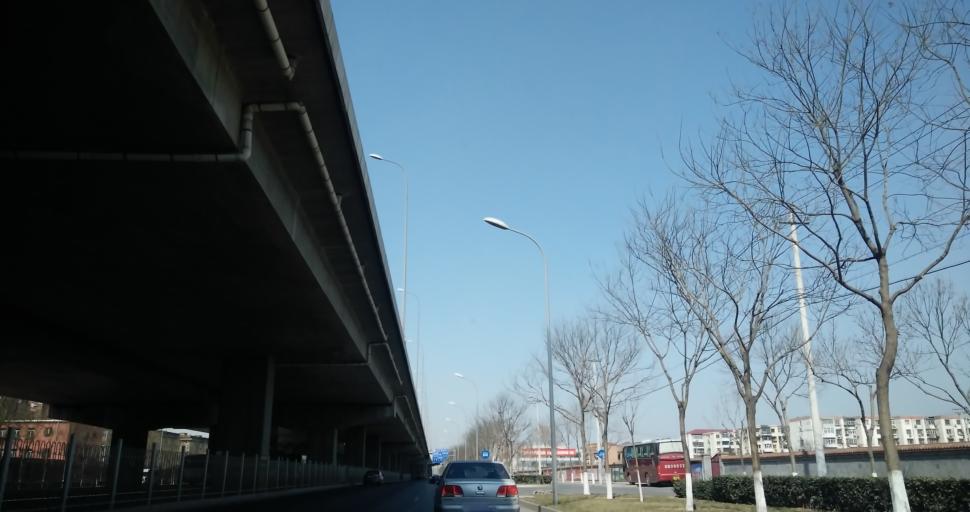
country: CN
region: Beijing
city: Jiugong
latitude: 39.7989
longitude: 116.4239
